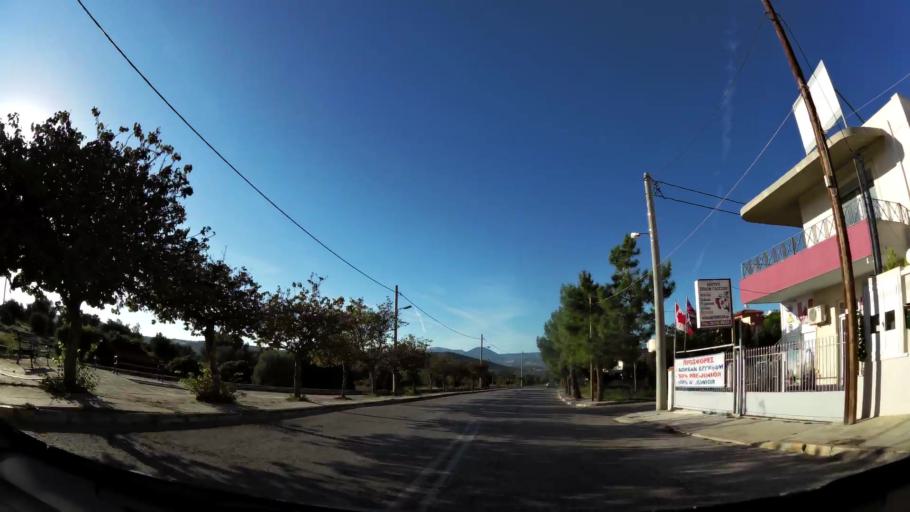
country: GR
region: Attica
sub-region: Nomarchia Anatolikis Attikis
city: Kalyvia Thorikou
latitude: 37.8356
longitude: 23.9243
